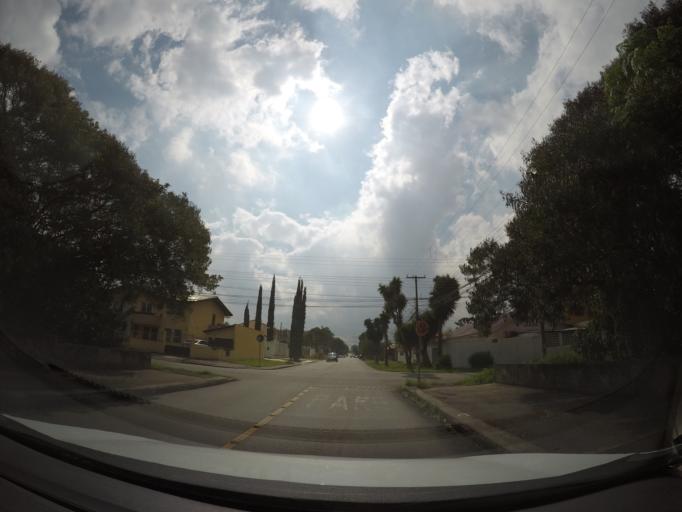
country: BR
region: Parana
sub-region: Sao Jose Dos Pinhais
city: Sao Jose dos Pinhais
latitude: -25.4879
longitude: -49.2482
